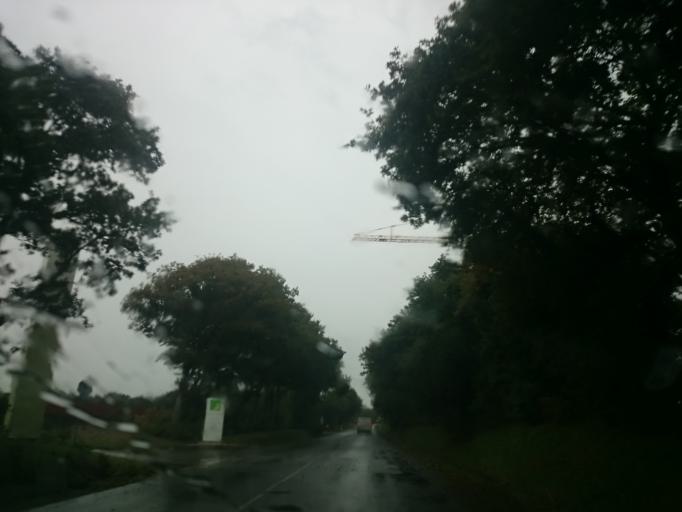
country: FR
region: Brittany
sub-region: Departement du Finistere
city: Gouesnou
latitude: 48.4621
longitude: -4.4532
